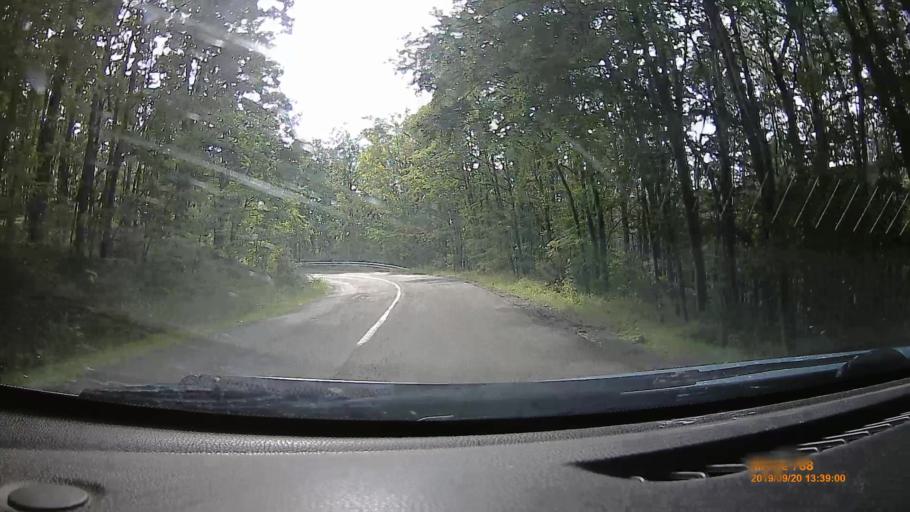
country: HU
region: Heves
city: Szilvasvarad
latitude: 48.0592
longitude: 20.5277
